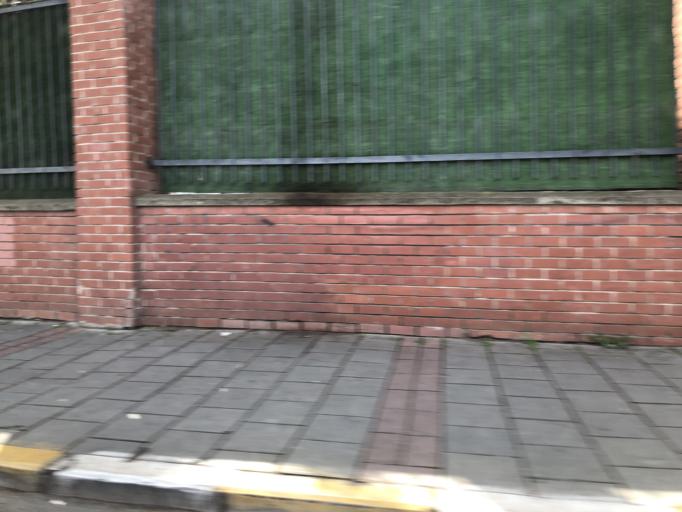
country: TR
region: Izmir
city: Karabaglar
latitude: 38.3896
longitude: 27.0453
